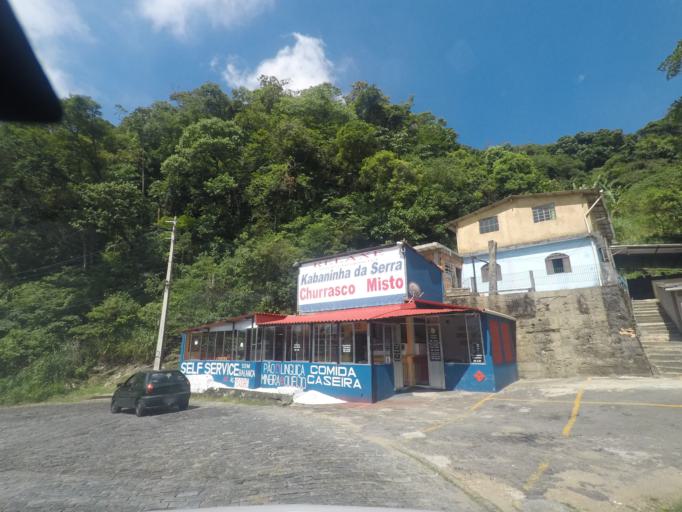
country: BR
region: Rio de Janeiro
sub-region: Petropolis
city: Petropolis
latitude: -22.5403
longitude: -43.1807
